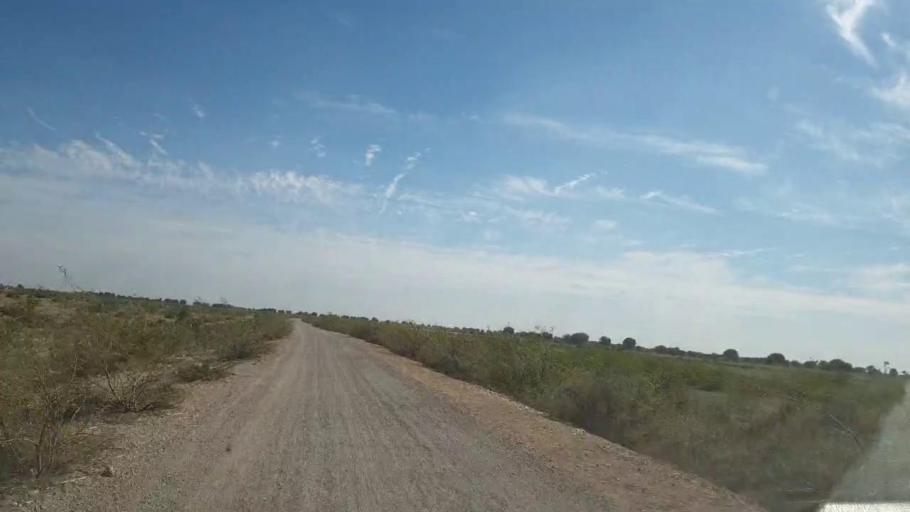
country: PK
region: Sindh
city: Pithoro
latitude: 25.5610
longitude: 69.3024
